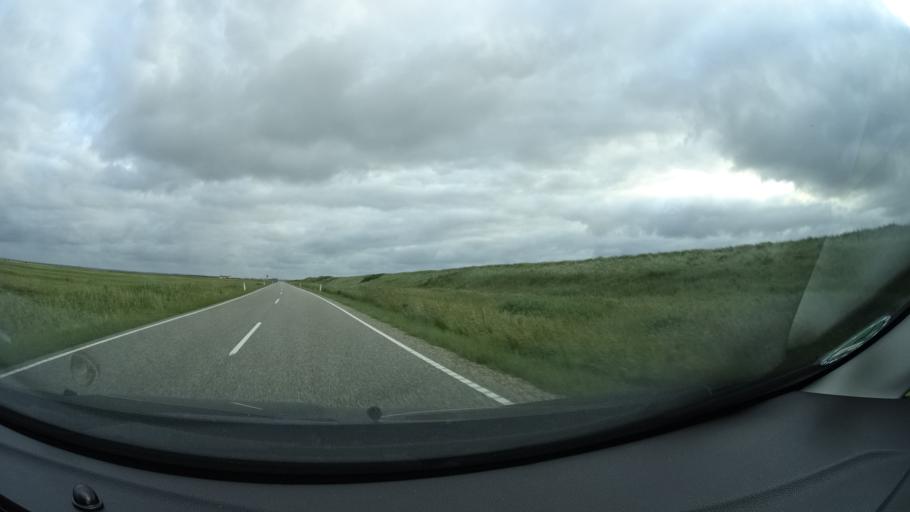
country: DK
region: Central Jutland
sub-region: Lemvig Kommune
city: Harboore
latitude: 56.3950
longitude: 8.1213
